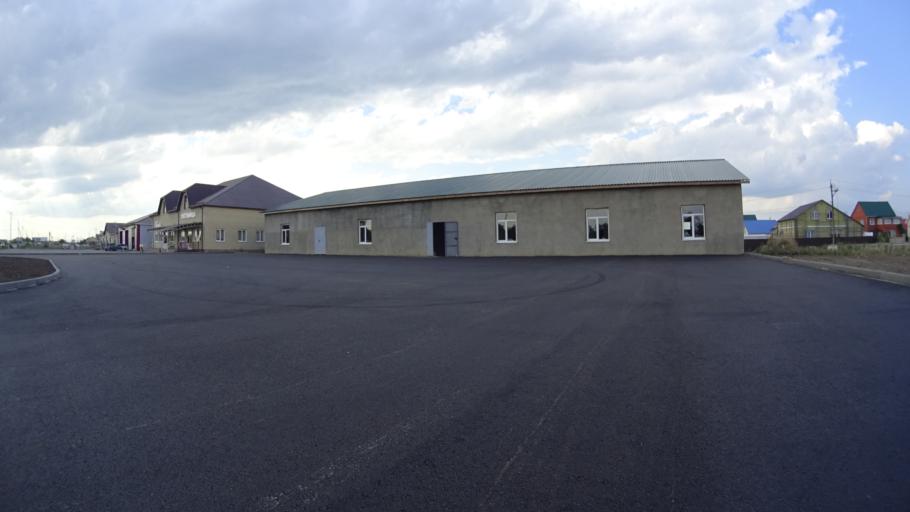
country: RU
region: Chelyabinsk
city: Troitsk
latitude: 54.0837
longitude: 61.5098
